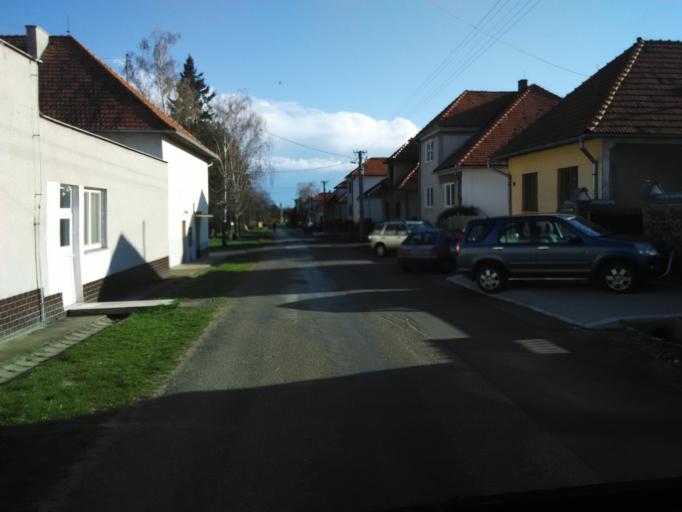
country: SK
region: Nitriansky
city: Tlmace
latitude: 48.2894
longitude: 18.5989
